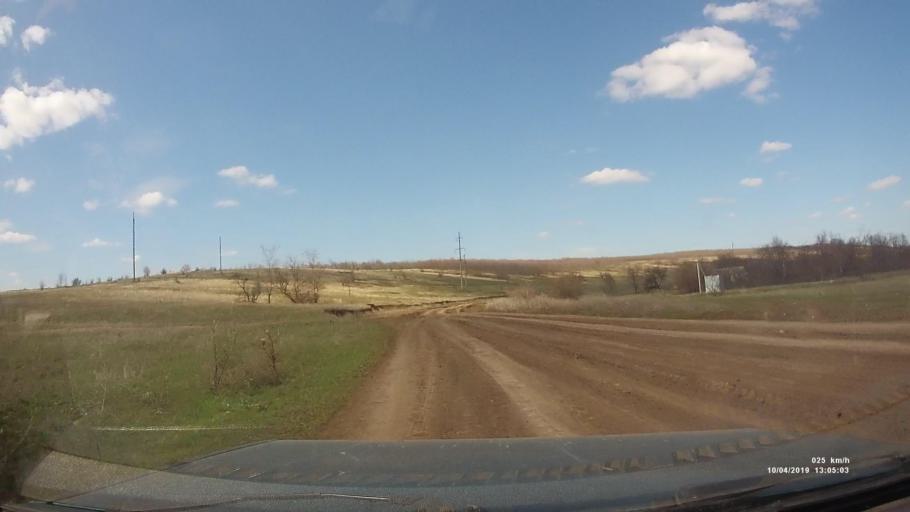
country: RU
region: Rostov
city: Masalovka
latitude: 48.3867
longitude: 40.2343
